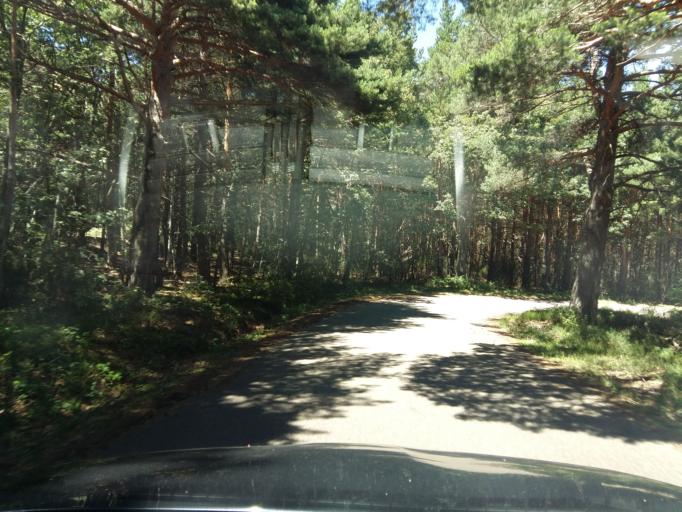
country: ES
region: Castille and Leon
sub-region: Provincia de Soria
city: Vozmediano
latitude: 41.8170
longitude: -1.8261
